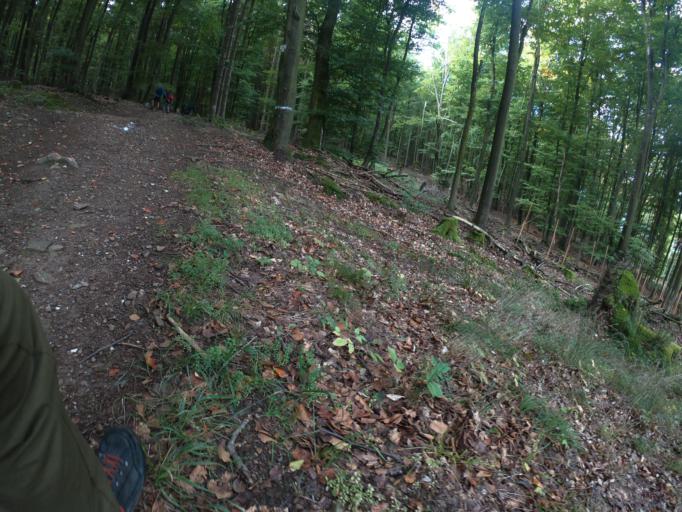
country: DE
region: Hesse
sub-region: Regierungsbezirk Darmstadt
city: Niedernhausen
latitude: 50.1499
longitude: 8.2948
